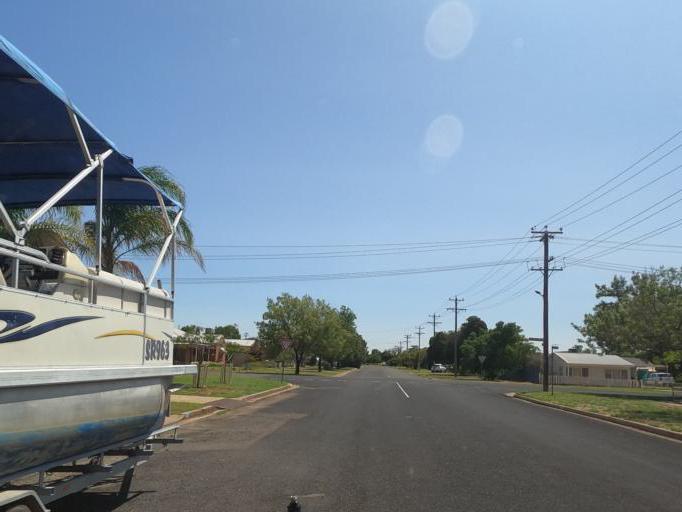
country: AU
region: New South Wales
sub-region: Corowa Shire
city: Mulwala
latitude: -35.9859
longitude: 146.0068
